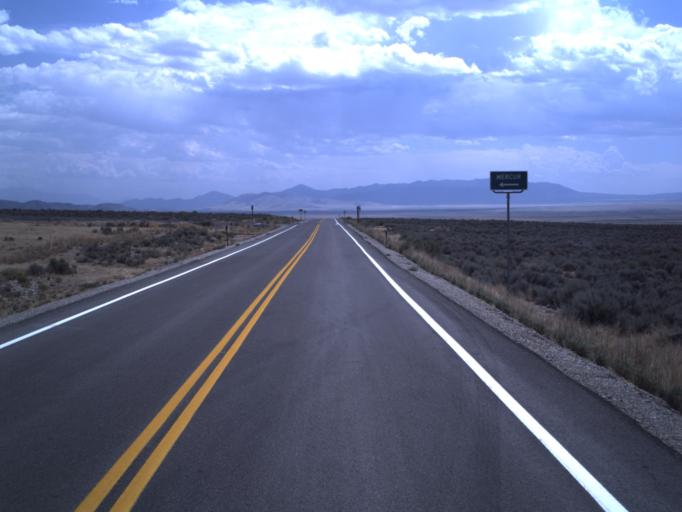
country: US
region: Utah
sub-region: Tooele County
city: Tooele
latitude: 40.2995
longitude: -112.2759
